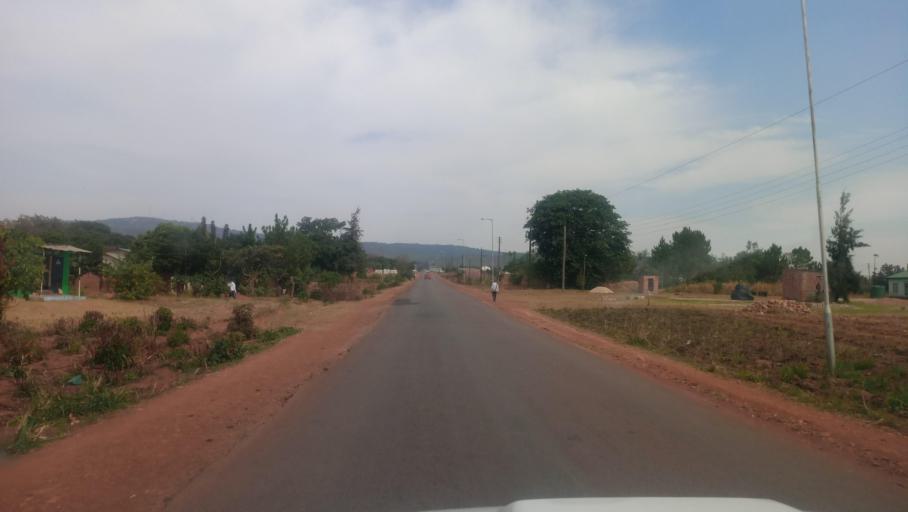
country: ZM
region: Northern
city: Mpika
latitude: -11.8394
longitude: 31.4352
